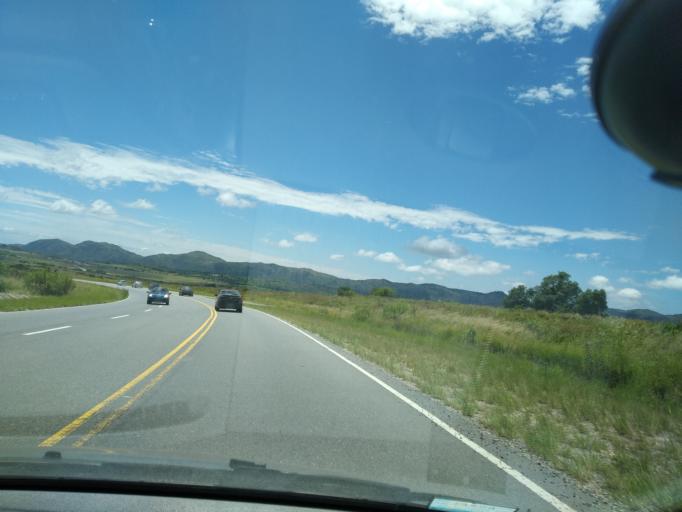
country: AR
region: Cordoba
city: Cuesta Blanca
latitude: -31.5872
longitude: -64.6170
